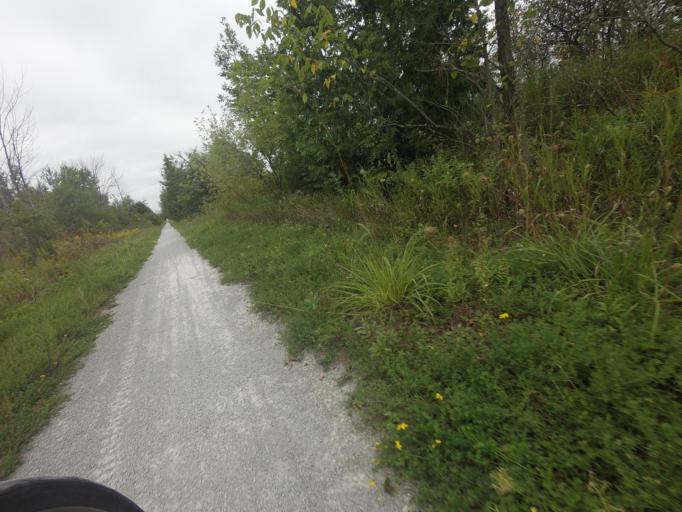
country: CA
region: Ontario
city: Omemee
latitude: 44.3251
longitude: -78.8106
